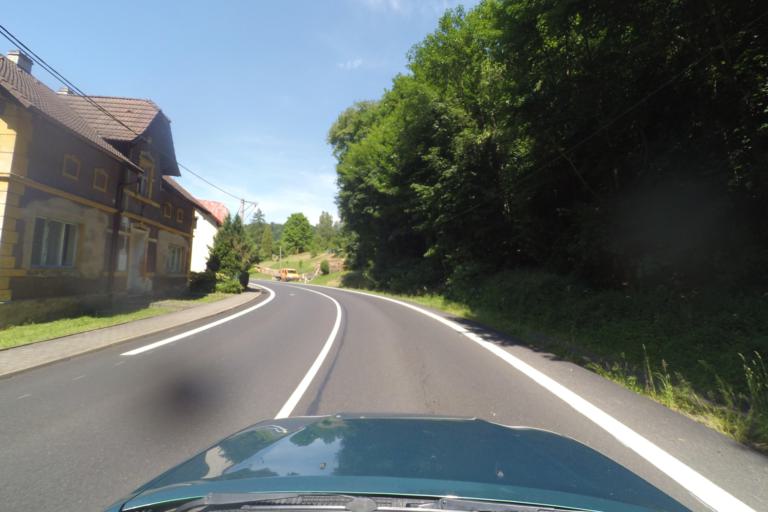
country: CZ
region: Ustecky
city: Benesov nad Ploucnici
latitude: 50.7223
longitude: 14.3244
